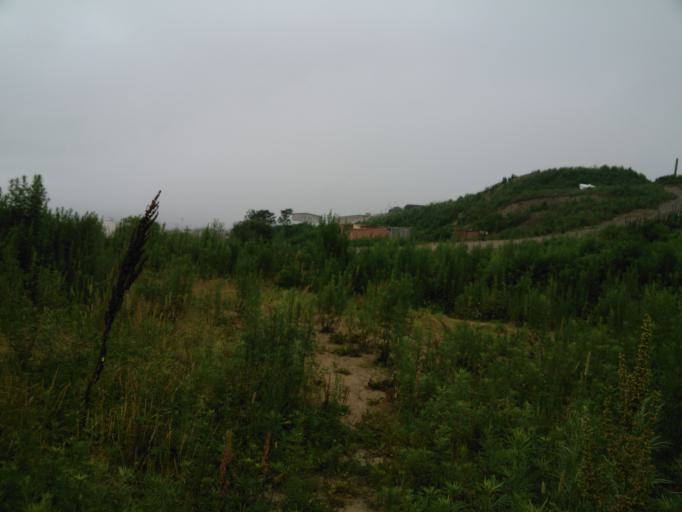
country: RU
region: Primorskiy
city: Vladivostok
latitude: 43.0956
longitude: 131.9855
